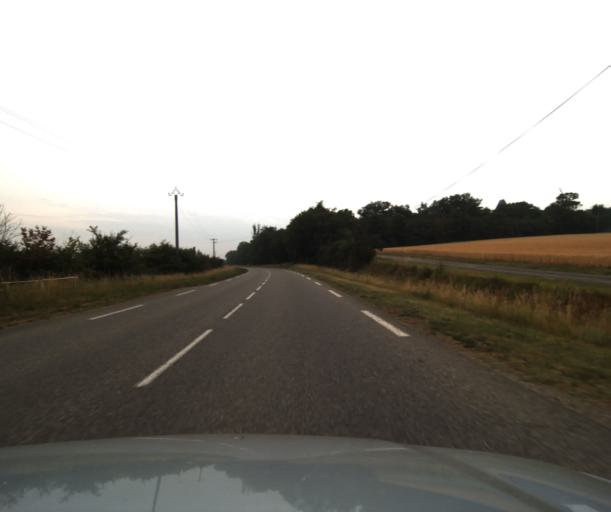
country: FR
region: Midi-Pyrenees
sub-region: Departement du Tarn-et-Garonne
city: Beaumont-de-Lomagne
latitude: 43.8633
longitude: 0.9532
